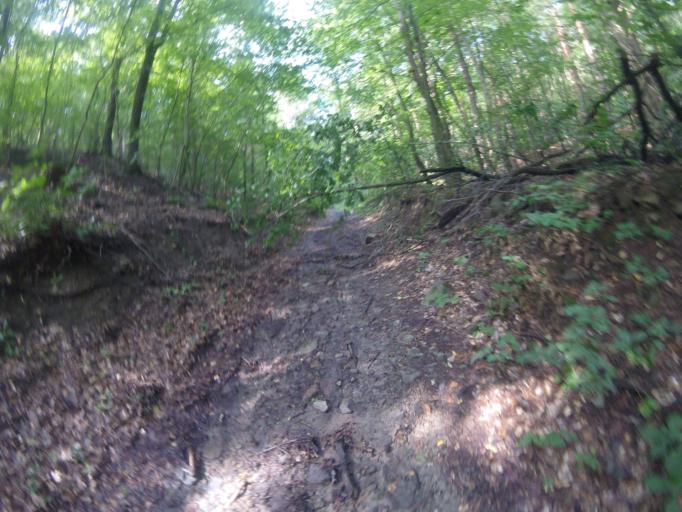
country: HU
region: Borsod-Abauj-Zemplen
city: Satoraljaujhely
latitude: 48.4561
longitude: 21.5806
